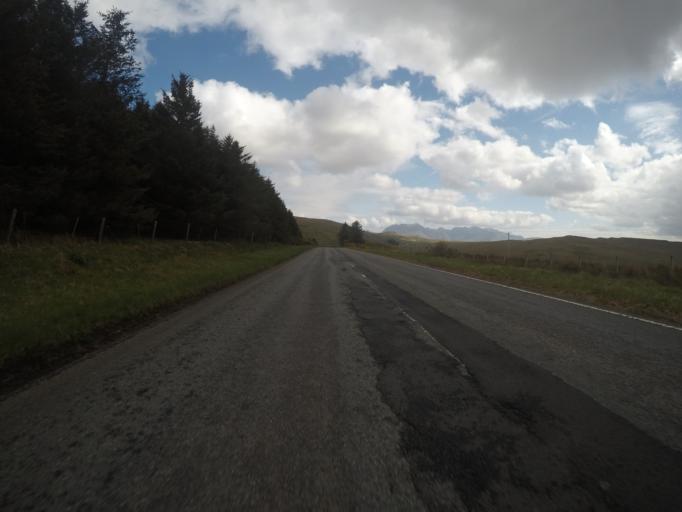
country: GB
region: Scotland
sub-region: Highland
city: Isle of Skye
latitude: 57.3322
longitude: -6.3455
